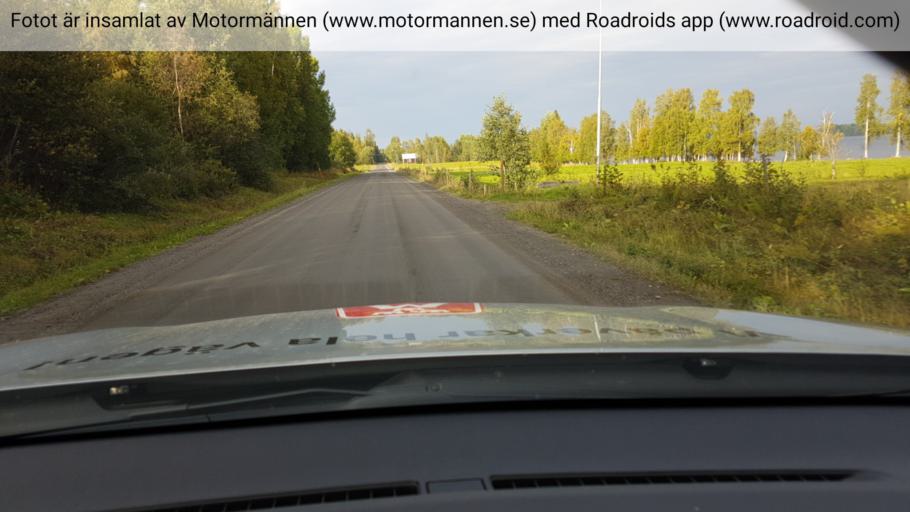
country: SE
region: Jaemtland
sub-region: Stroemsunds Kommun
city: Stroemsund
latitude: 64.0350
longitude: 15.8096
